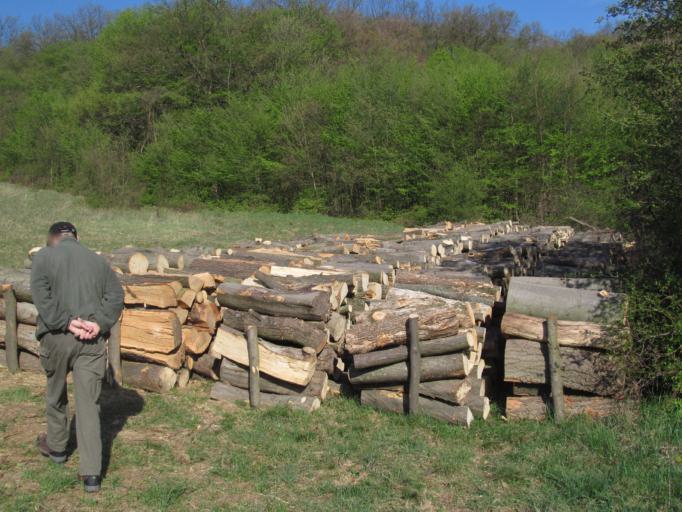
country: HU
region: Veszprem
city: Zanka
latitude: 46.9471
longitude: 17.5907
